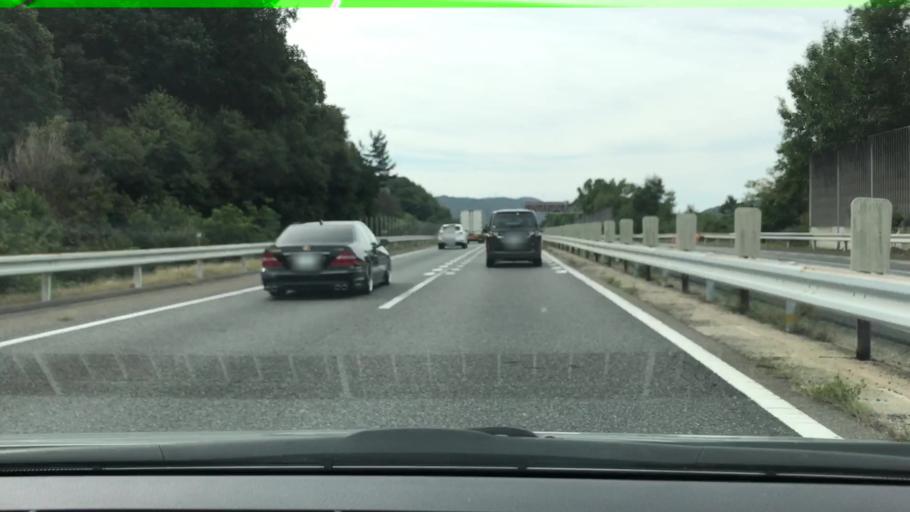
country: JP
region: Hyogo
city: Aioi
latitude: 34.8162
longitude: 134.4580
